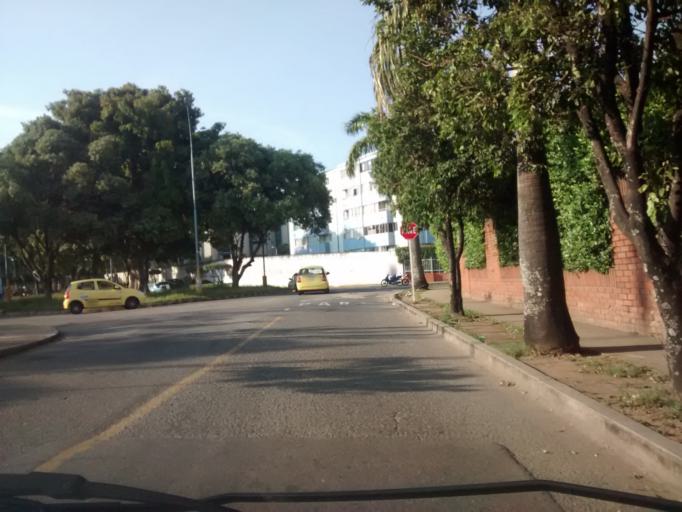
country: CO
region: Santander
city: Bucaramanga
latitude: 7.0985
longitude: -73.1271
